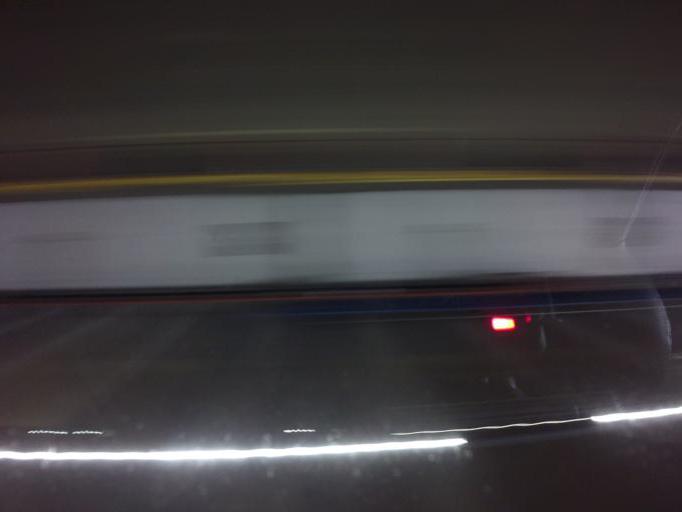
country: PH
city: Sambayanihan People's Village
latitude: 14.5160
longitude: 120.9792
